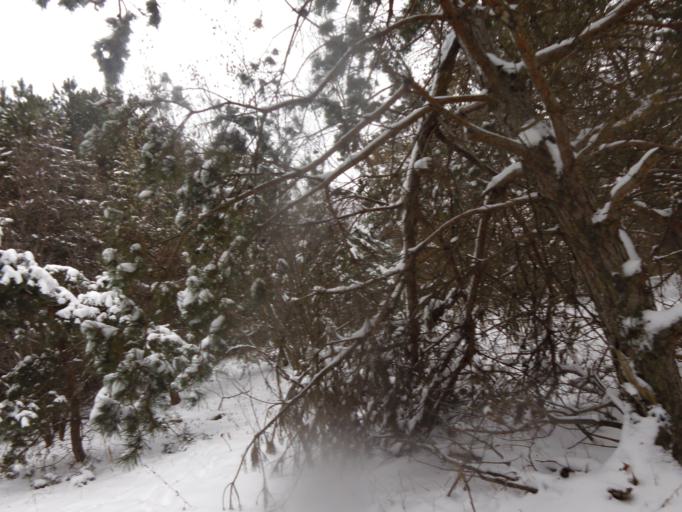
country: US
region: Minnesota
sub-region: Dakota County
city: Inver Grove Heights
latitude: 44.8598
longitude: -93.0732
